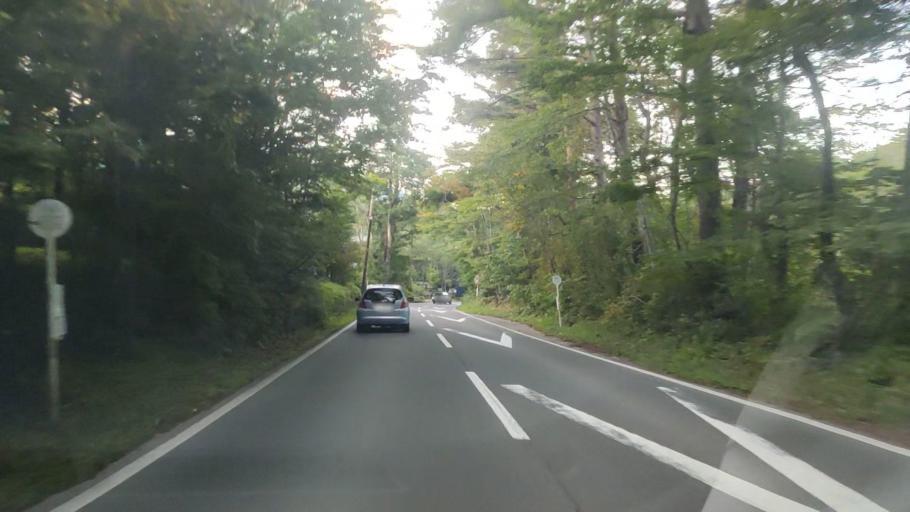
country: JP
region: Nagano
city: Komoro
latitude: 36.3774
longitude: 138.5864
